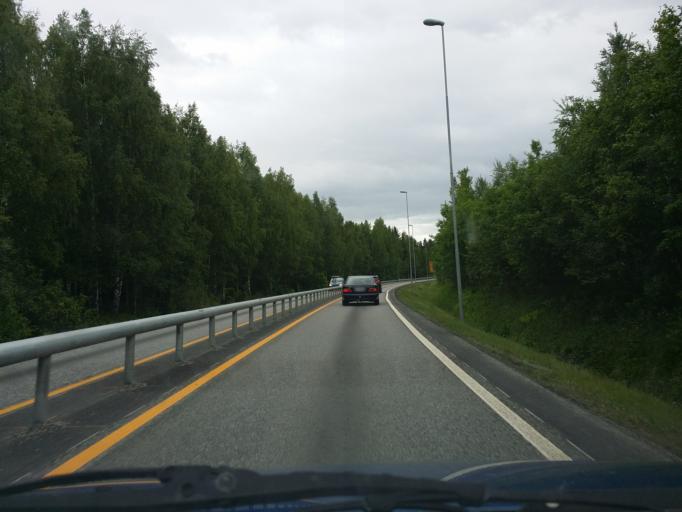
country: NO
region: Hedmark
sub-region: Ringsaker
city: Moelv
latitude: 60.9628
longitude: 10.6194
